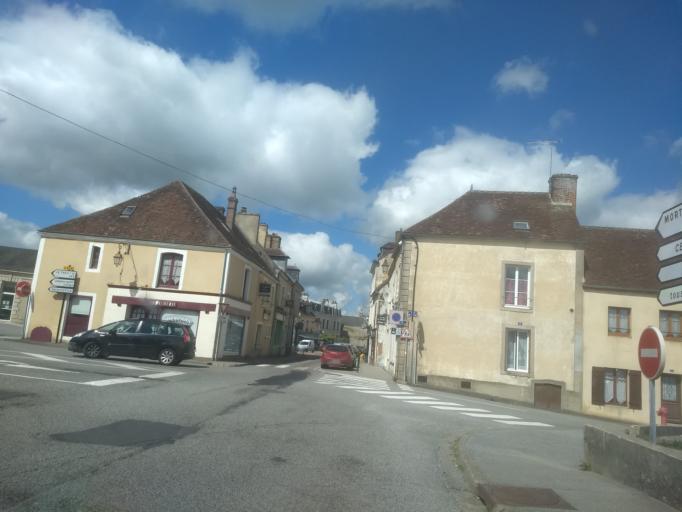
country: FR
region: Lower Normandy
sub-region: Departement de l'Orne
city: Belleme
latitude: 48.3747
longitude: 0.5679
